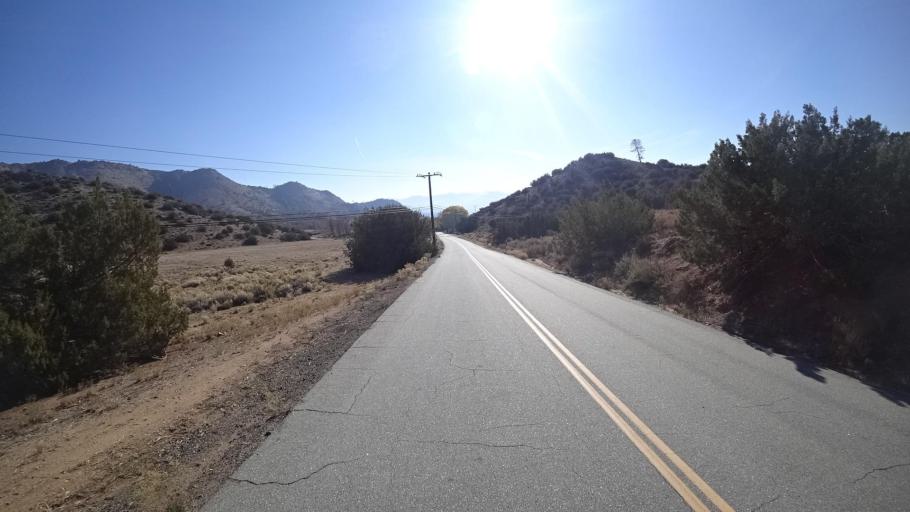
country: US
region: California
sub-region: Kern County
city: Tehachapi
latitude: 35.3662
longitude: -118.3850
